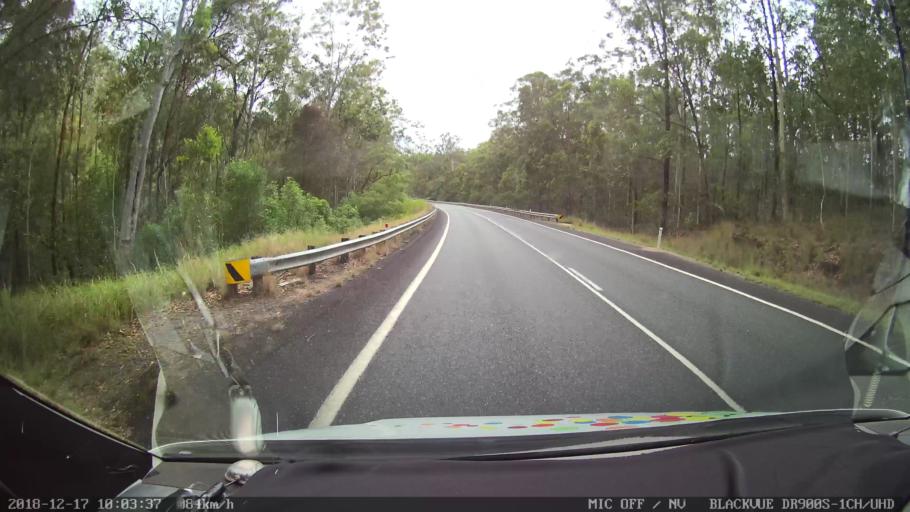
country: AU
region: New South Wales
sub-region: Tenterfield Municipality
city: Carrolls Creek
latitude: -28.8971
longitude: 152.4667
